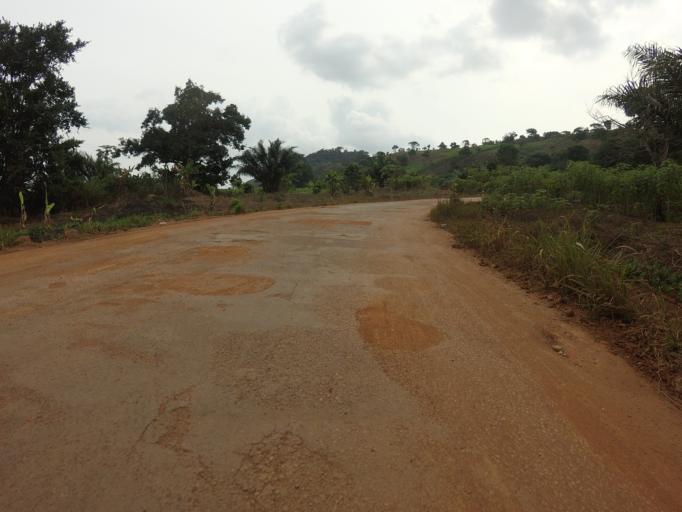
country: GH
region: Volta
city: Ho
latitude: 6.6792
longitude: 0.3502
